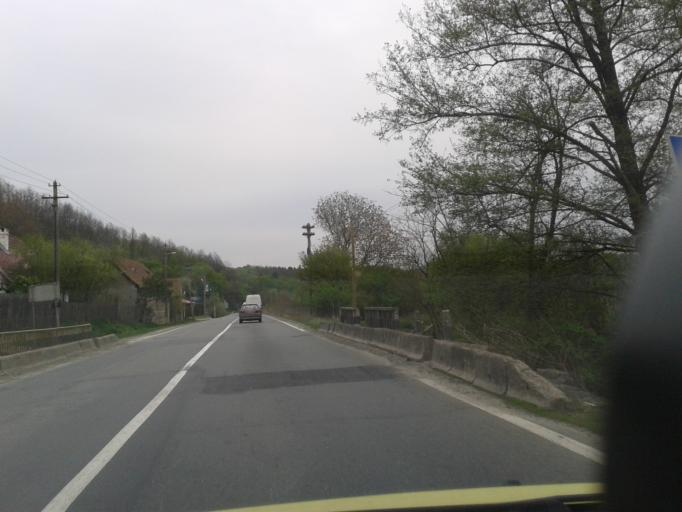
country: RO
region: Arad
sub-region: Comuna Barzava
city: Barzava
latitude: 46.1013
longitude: 22.0093
